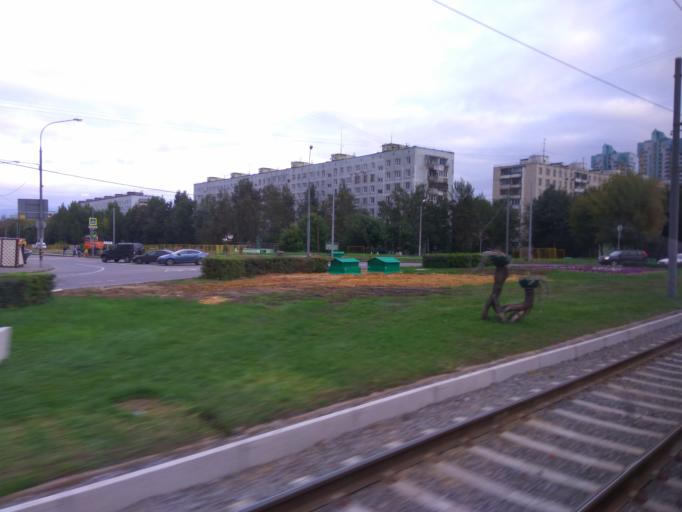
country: RU
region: Moscow
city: Chertanovo Yuzhnoye
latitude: 55.6129
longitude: 37.5919
